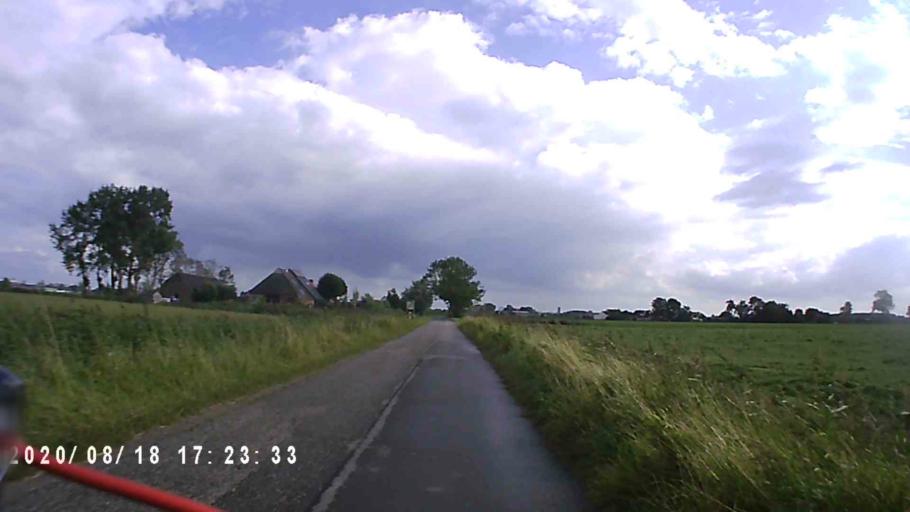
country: NL
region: Groningen
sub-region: Gemeente Zuidhorn
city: Aduard
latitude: 53.2478
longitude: 6.4885
